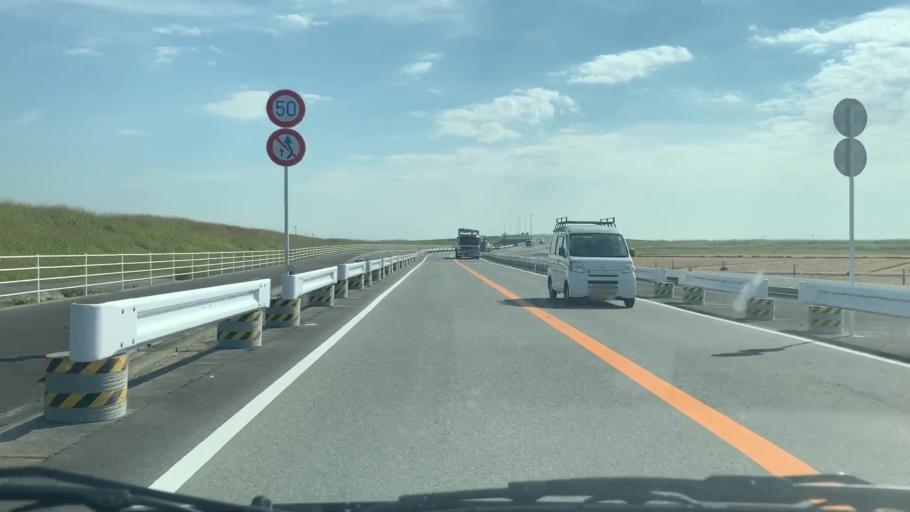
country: JP
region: Saga Prefecture
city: Saga-shi
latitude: 33.2243
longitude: 130.1896
